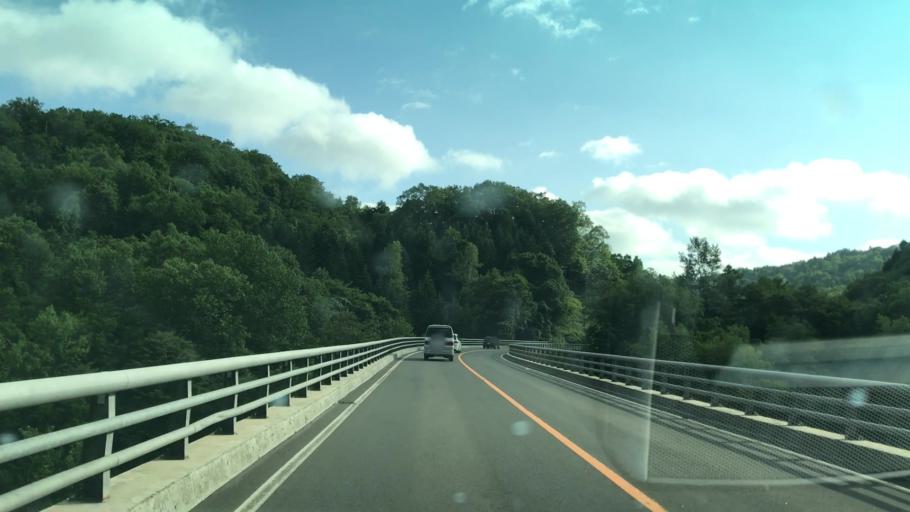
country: JP
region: Hokkaido
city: Shimo-furano
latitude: 42.8878
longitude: 142.2379
